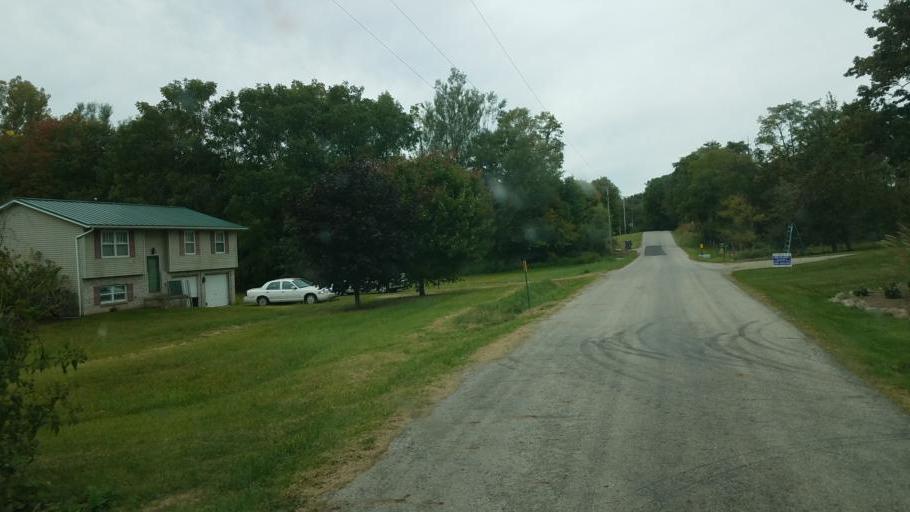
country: US
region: Ohio
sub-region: Knox County
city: Centerburg
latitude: 40.3331
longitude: -82.6637
